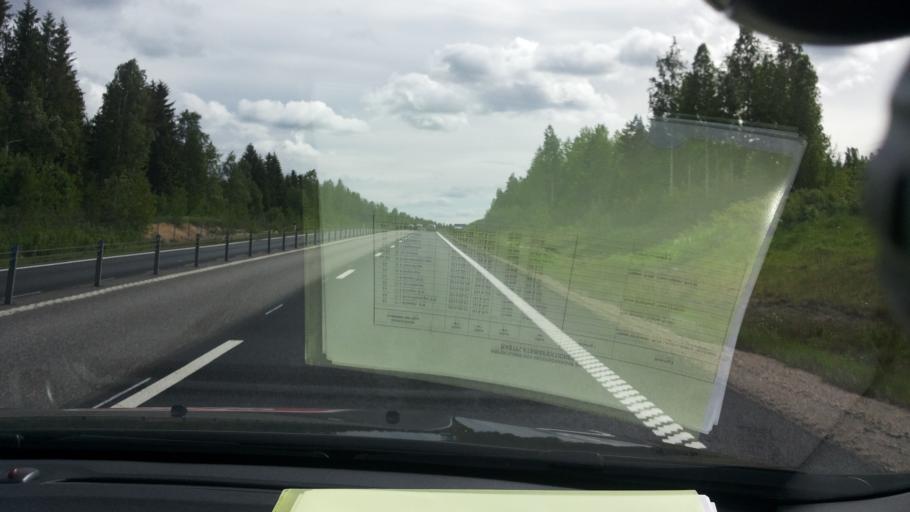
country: SE
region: Vaesternorrland
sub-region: Sundsvalls Kommun
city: Njurundabommen
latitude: 62.1833
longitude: 17.3564
